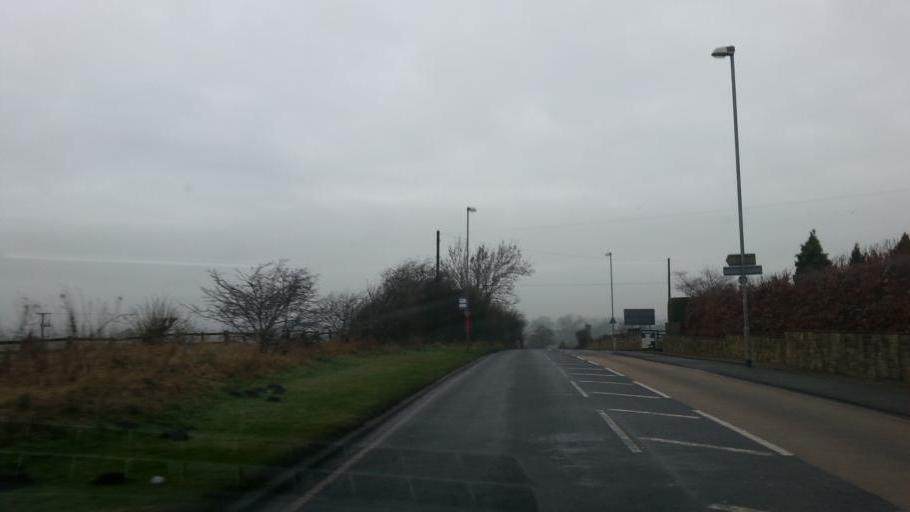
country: GB
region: England
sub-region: City and Borough of Wakefield
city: Badsworth
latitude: 53.6416
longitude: -1.2783
